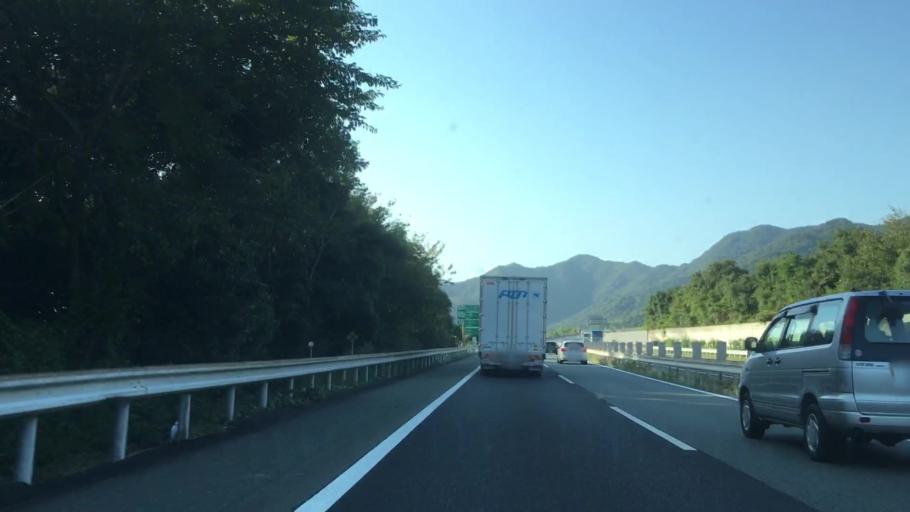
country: JP
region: Yamaguchi
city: Ogori-shimogo
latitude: 34.0913
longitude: 131.4579
